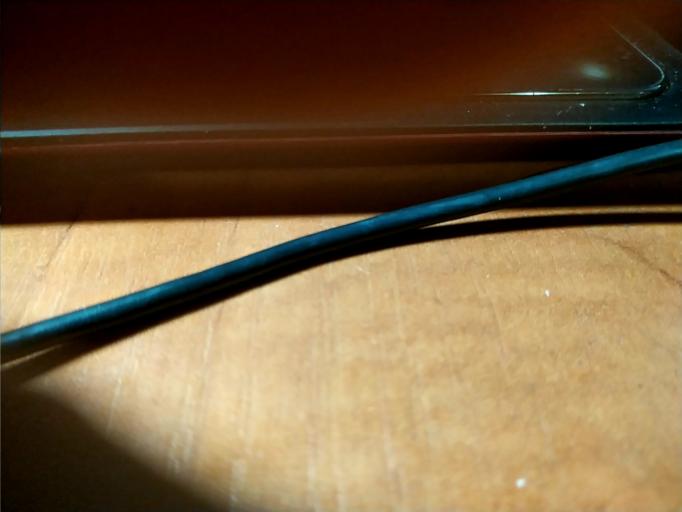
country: RU
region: Tverskaya
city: Sakharovo
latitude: 56.8132
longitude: 35.9937
